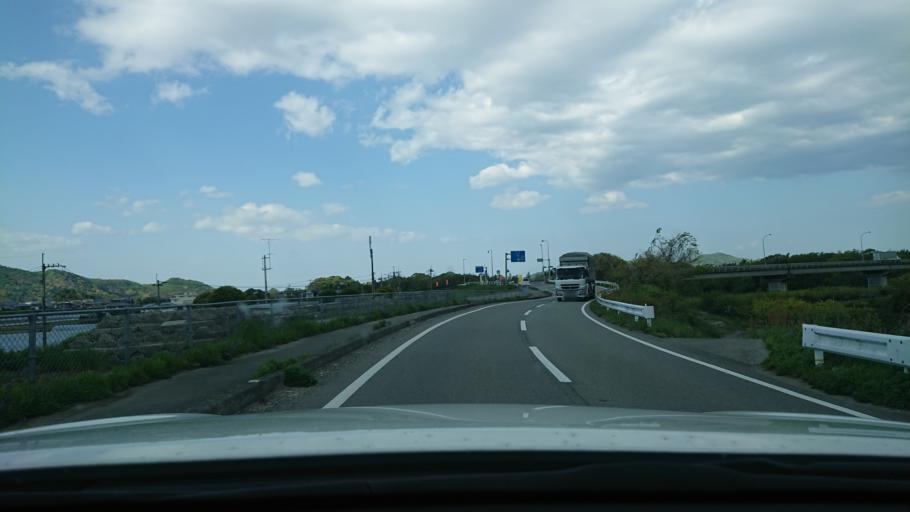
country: JP
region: Tokushima
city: Komatsushimacho
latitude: 33.9939
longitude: 134.5463
